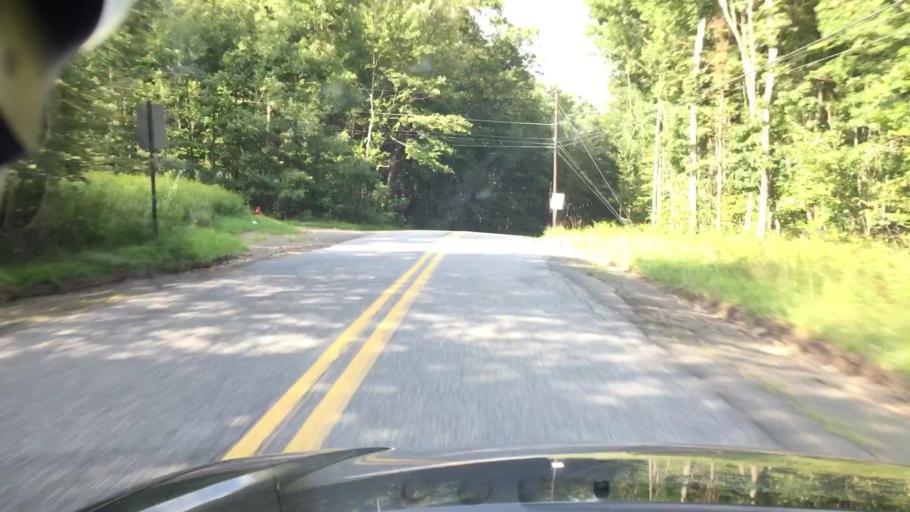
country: US
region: Pennsylvania
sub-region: Luzerne County
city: Harleigh
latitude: 41.0553
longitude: -75.9693
